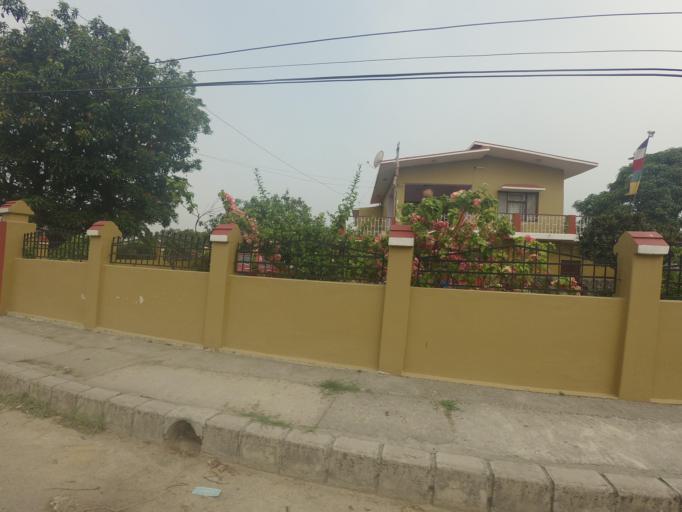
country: NP
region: Western Region
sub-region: Lumbini Zone
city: Bhairahawa
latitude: 27.4917
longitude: 83.4463
